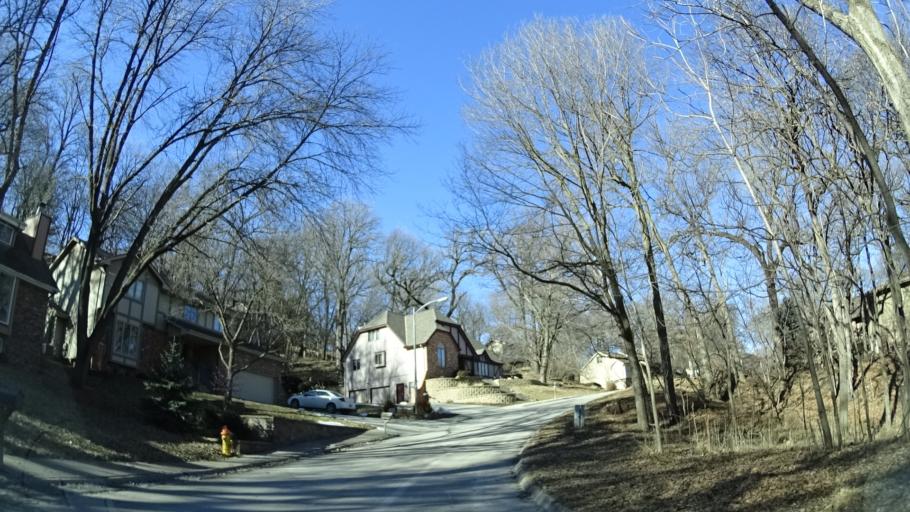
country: US
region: Nebraska
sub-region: Sarpy County
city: Bellevue
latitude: 41.1525
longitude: -95.8972
